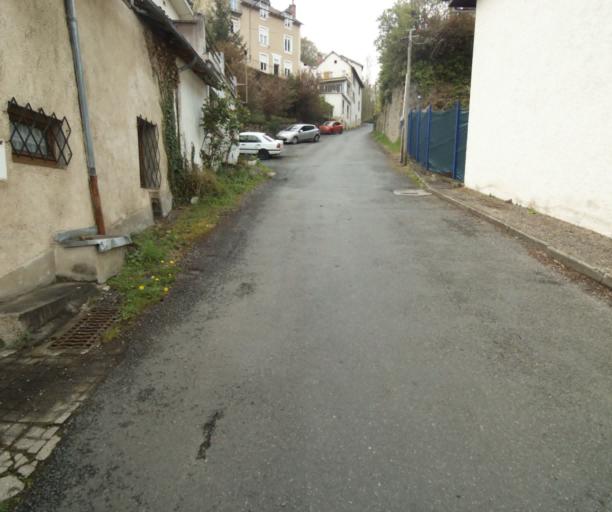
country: FR
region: Limousin
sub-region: Departement de la Correze
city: Tulle
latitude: 45.2616
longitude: 1.7545
